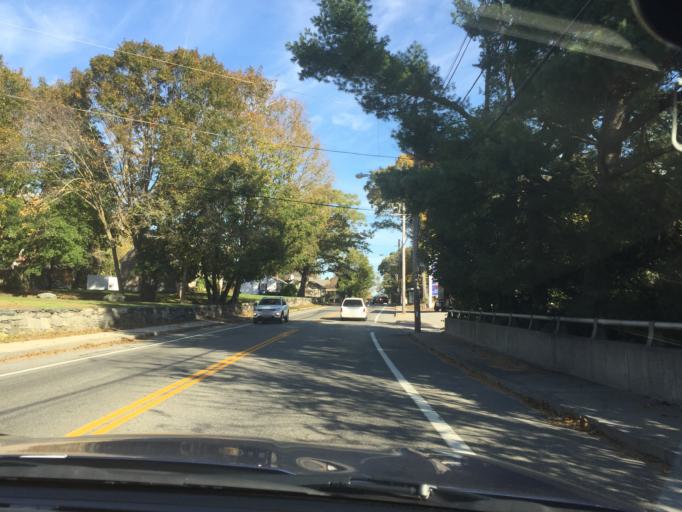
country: US
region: Rhode Island
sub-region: Kent County
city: East Greenwich
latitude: 41.6664
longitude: -71.4499
